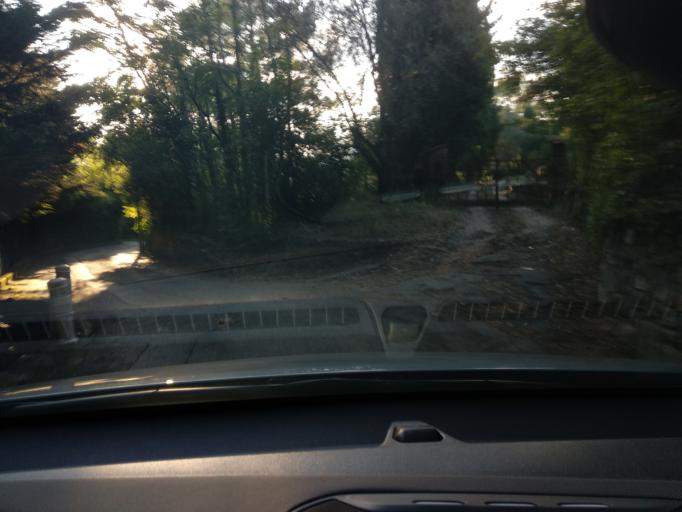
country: FR
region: Provence-Alpes-Cote d'Azur
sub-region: Departement des Alpes-Maritimes
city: Grasse
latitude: 43.6371
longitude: 6.9380
